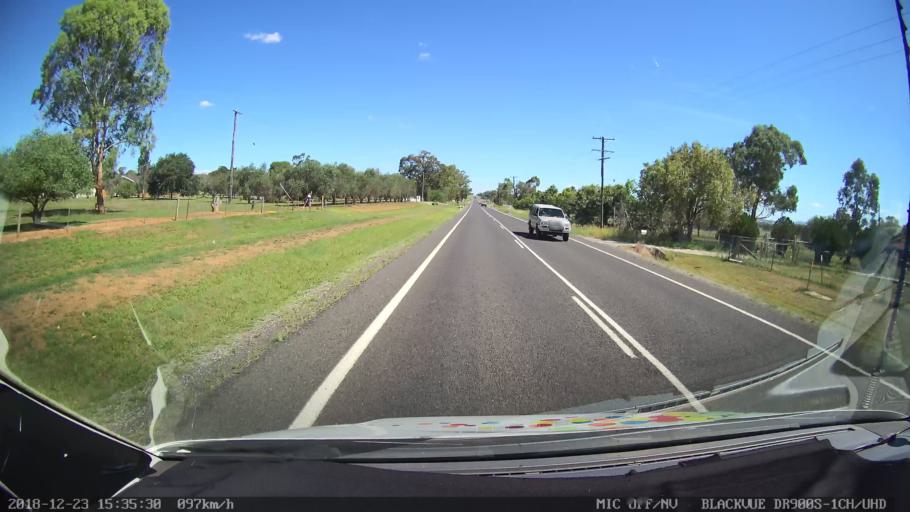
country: AU
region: New South Wales
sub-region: Tamworth Municipality
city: Tamworth
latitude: -31.0282
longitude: 150.8827
